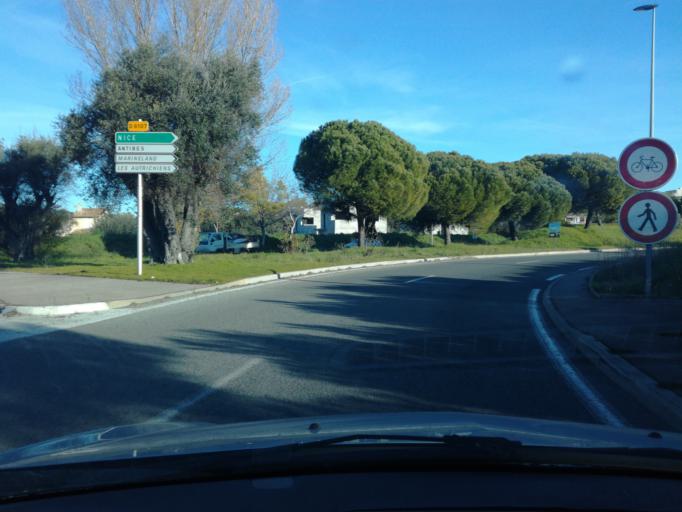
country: FR
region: Provence-Alpes-Cote d'Azur
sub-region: Departement des Alpes-Maritimes
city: Vallauris
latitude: 43.5786
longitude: 7.0912
